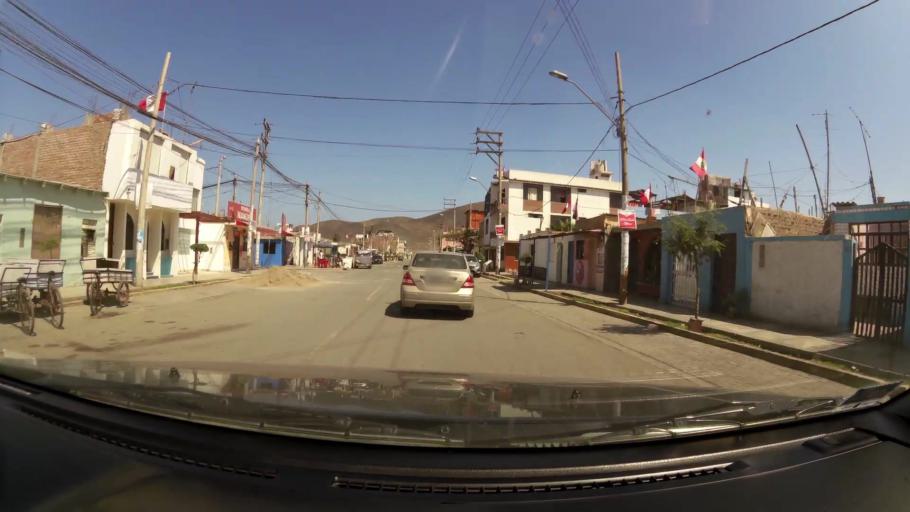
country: PE
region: Lima
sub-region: Provincia de Canete
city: San Vicente de Canete
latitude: -13.0266
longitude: -76.4806
